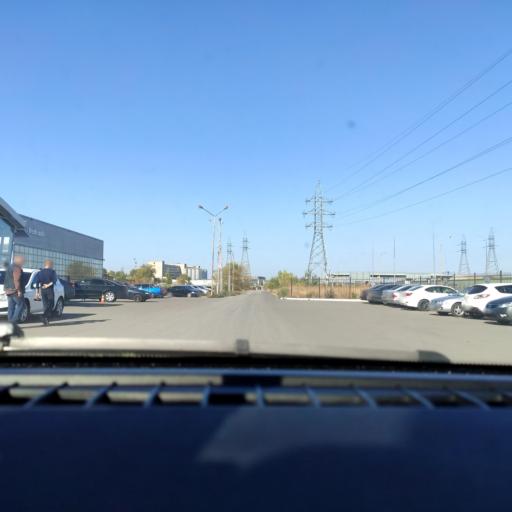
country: RU
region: Voronezj
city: Somovo
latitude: 51.6653
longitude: 39.3001
